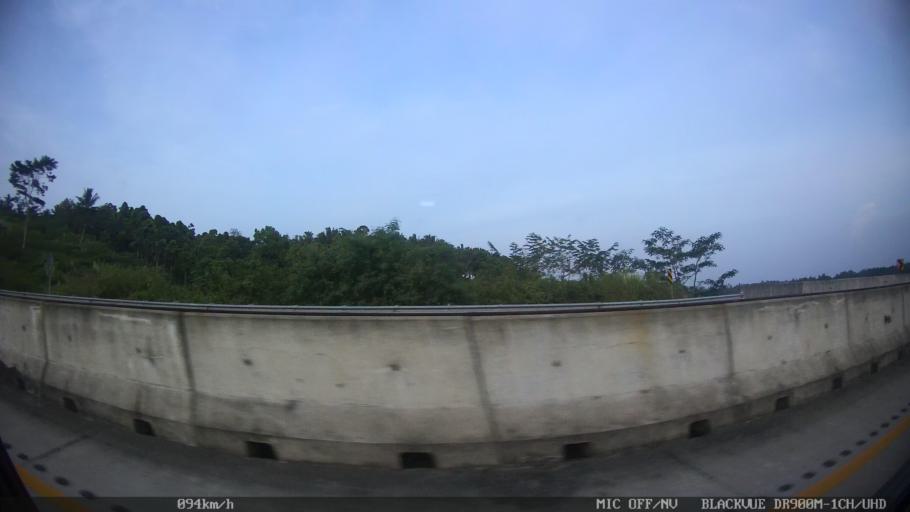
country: ID
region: Lampung
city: Penengahan
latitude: -5.8159
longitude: 105.7367
